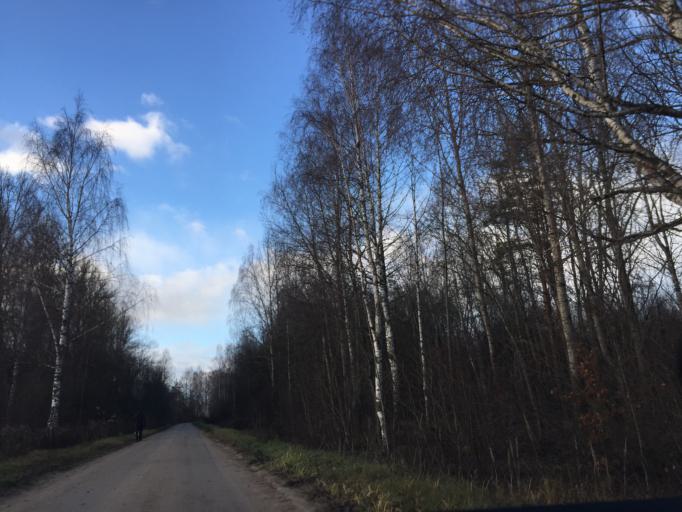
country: LV
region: Valmieras Rajons
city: Valmiera
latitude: 57.5377
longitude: 25.3864
